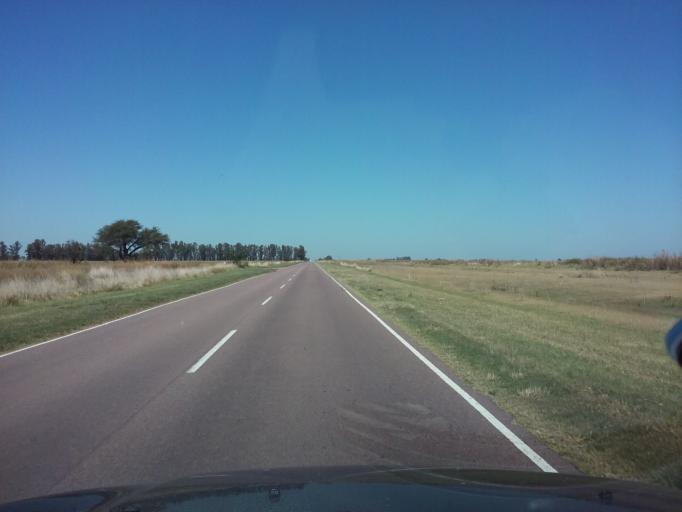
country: AR
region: La Pampa
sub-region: Departamento de Trenel
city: Trenel
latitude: -35.8690
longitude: -63.9401
